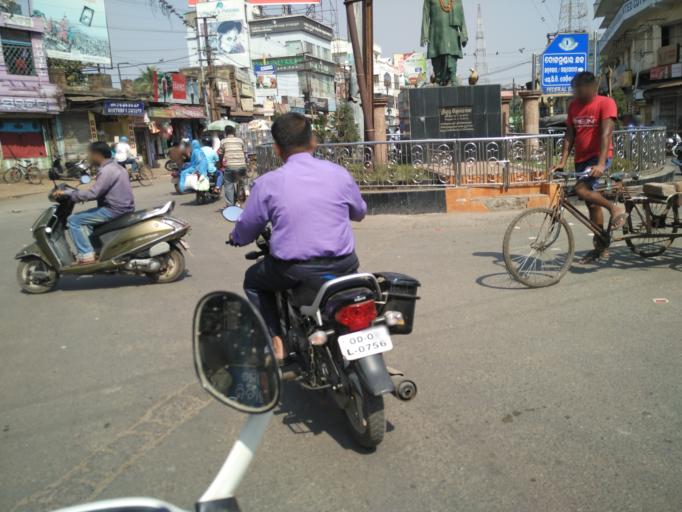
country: IN
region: Odisha
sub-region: Cuttack
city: Cuttack
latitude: 20.4624
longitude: 85.8831
